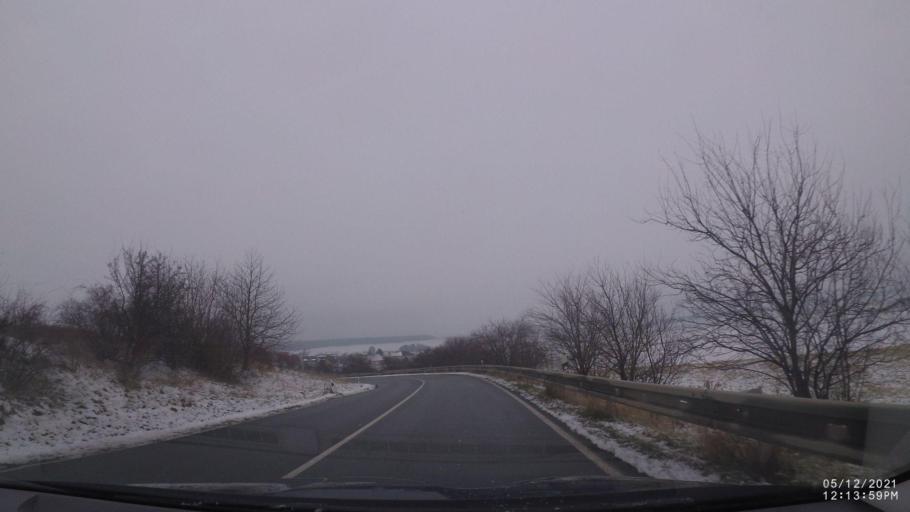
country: CZ
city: Ceske Mezirici
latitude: 50.3051
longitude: 16.0269
